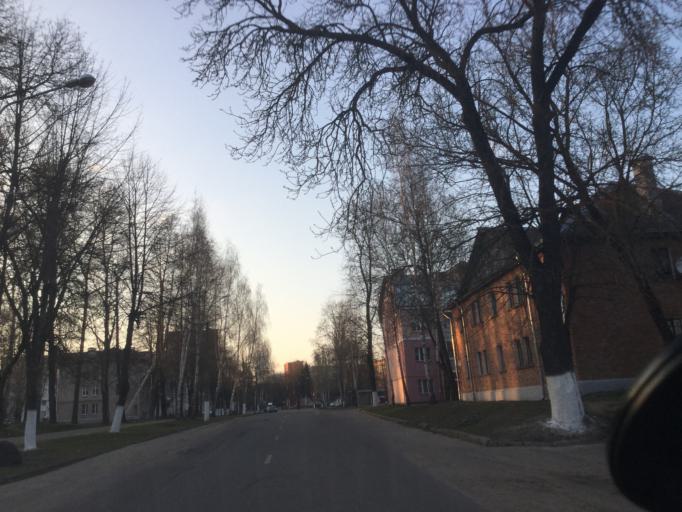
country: BY
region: Vitebsk
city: Vitebsk
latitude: 55.1656
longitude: 30.1308
